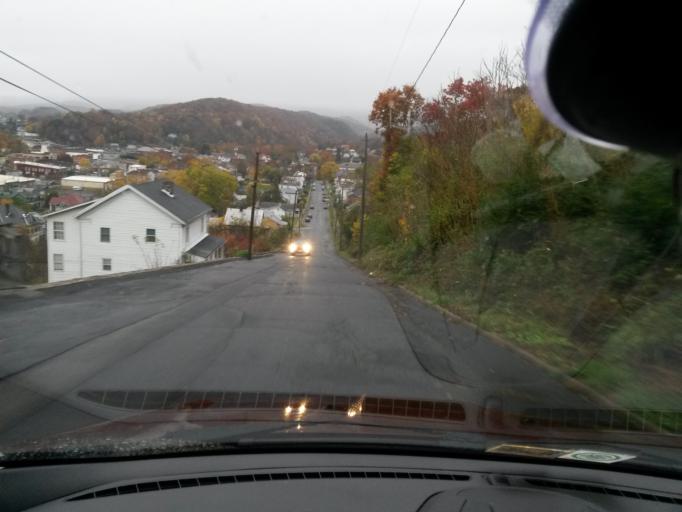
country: US
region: Virginia
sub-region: Alleghany County
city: Clifton Forge
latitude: 37.8169
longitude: -79.8178
